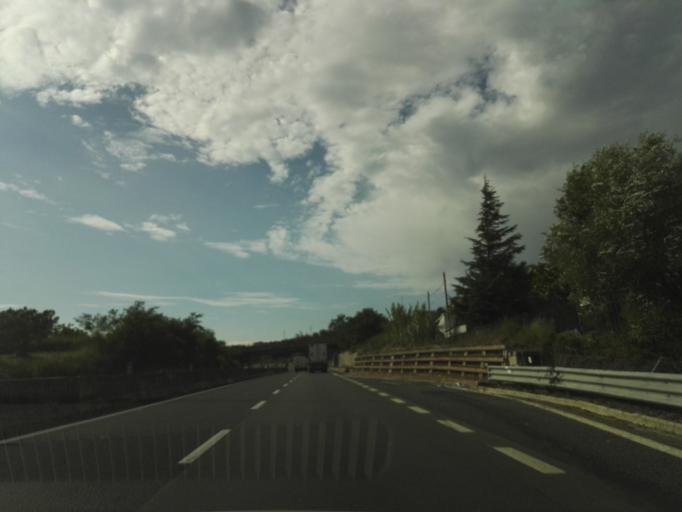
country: IT
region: Calabria
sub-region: Provincia di Catanzaro
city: Marcellinara
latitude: 38.9149
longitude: 16.4921
